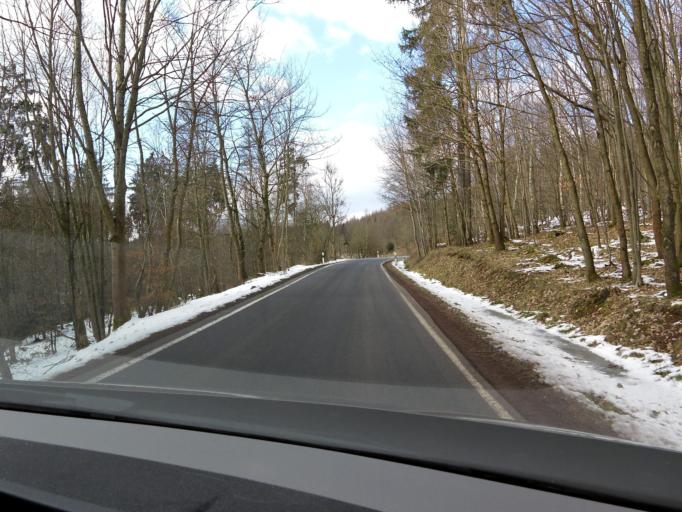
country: DE
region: Thuringia
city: Wolfsburg-Unkeroda
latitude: 50.8892
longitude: 10.2836
